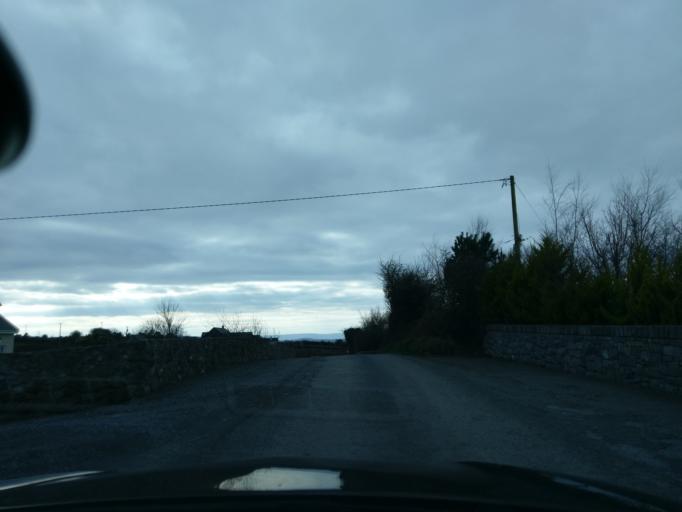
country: IE
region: Connaught
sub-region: County Galway
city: Oranmore
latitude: 53.2188
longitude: -8.8969
